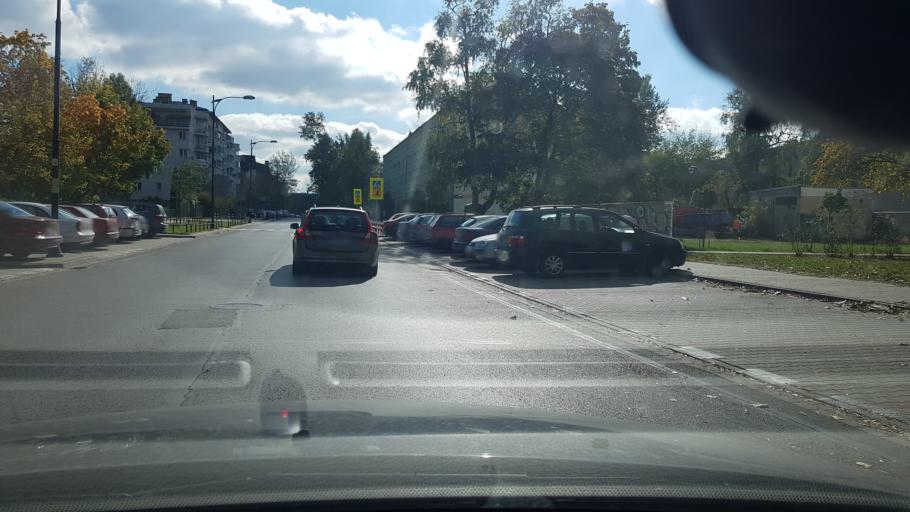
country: PL
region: Masovian Voivodeship
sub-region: Warszawa
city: Bielany
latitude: 52.2934
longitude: 20.9438
